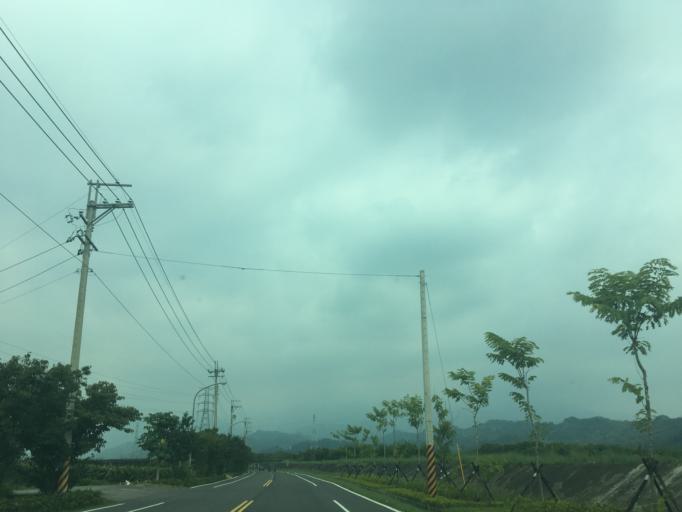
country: TW
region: Taiwan
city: Fengyuan
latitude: 24.2910
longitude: 120.8417
